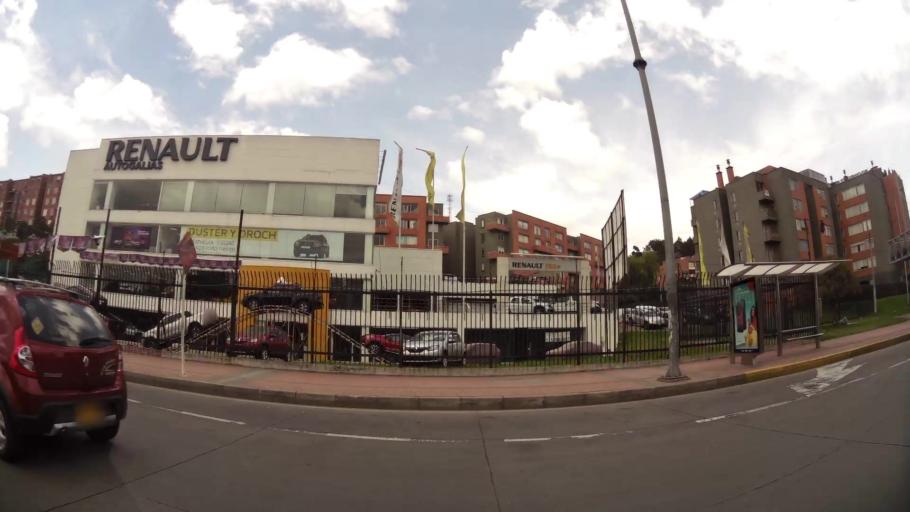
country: CO
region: Cundinamarca
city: Cota
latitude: 4.7350
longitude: -74.0803
